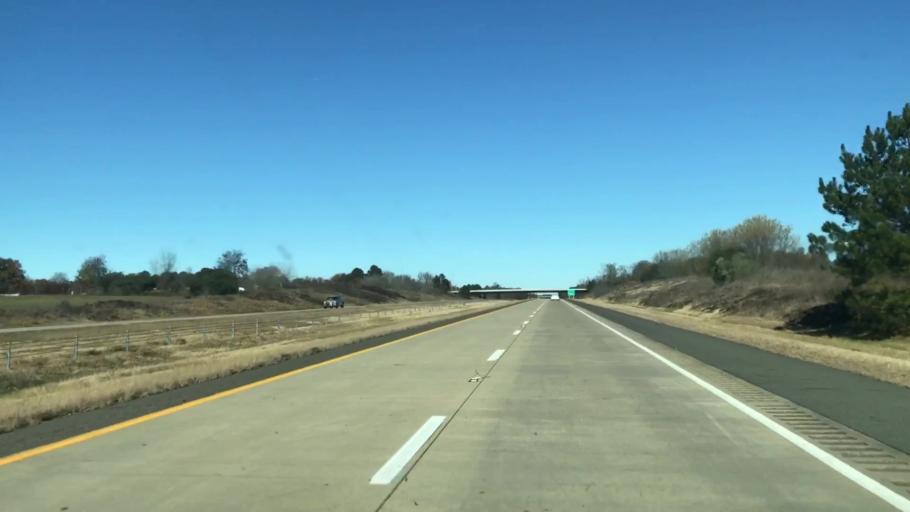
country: US
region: Texas
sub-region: Bowie County
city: Texarkana
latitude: 33.3125
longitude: -93.9415
